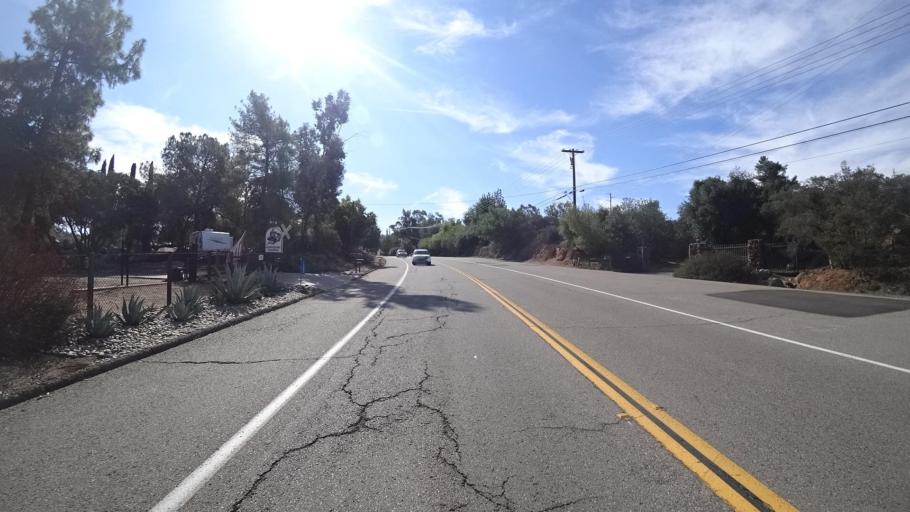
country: US
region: California
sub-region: San Diego County
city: Alpine
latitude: 32.8253
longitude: -116.7891
